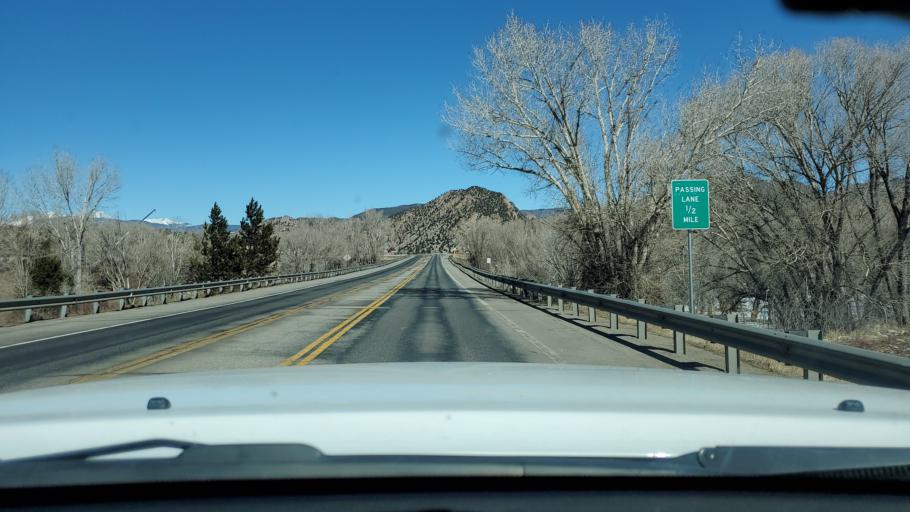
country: US
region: Colorado
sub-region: Chaffee County
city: Buena Vista
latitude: 38.7395
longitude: -106.0828
